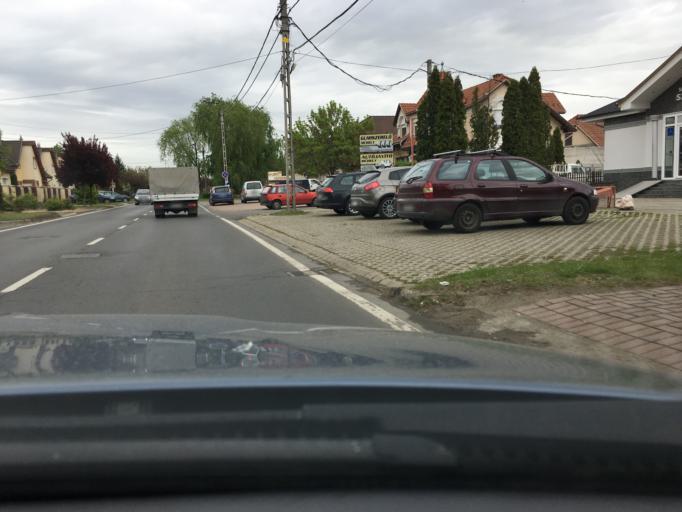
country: HU
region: Hajdu-Bihar
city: Debrecen
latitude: 47.5369
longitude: 21.6713
